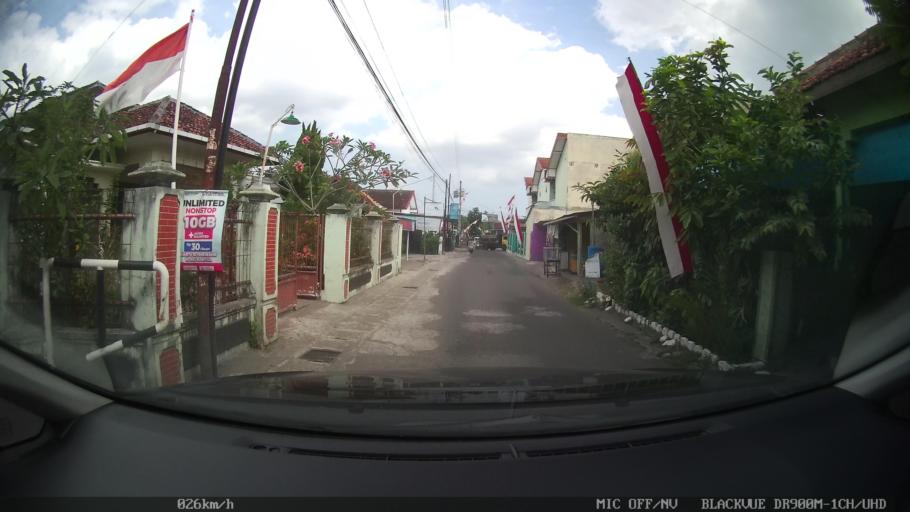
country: ID
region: Daerah Istimewa Yogyakarta
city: Gamping Lor
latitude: -7.8058
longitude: 110.3279
